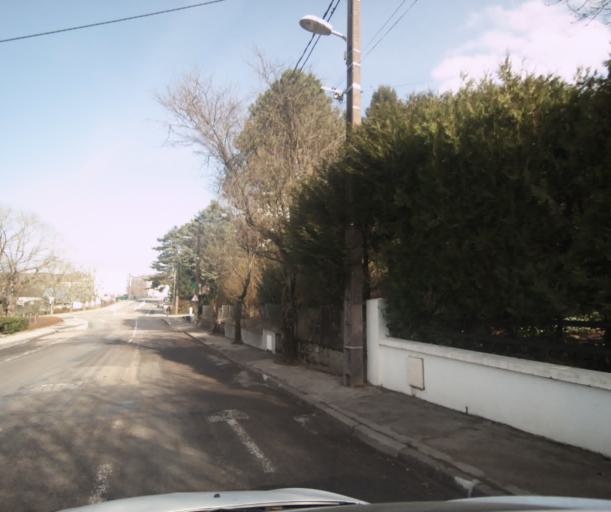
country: FR
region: Franche-Comte
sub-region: Departement du Doubs
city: Montfaucon
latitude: 47.2474
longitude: 6.0571
